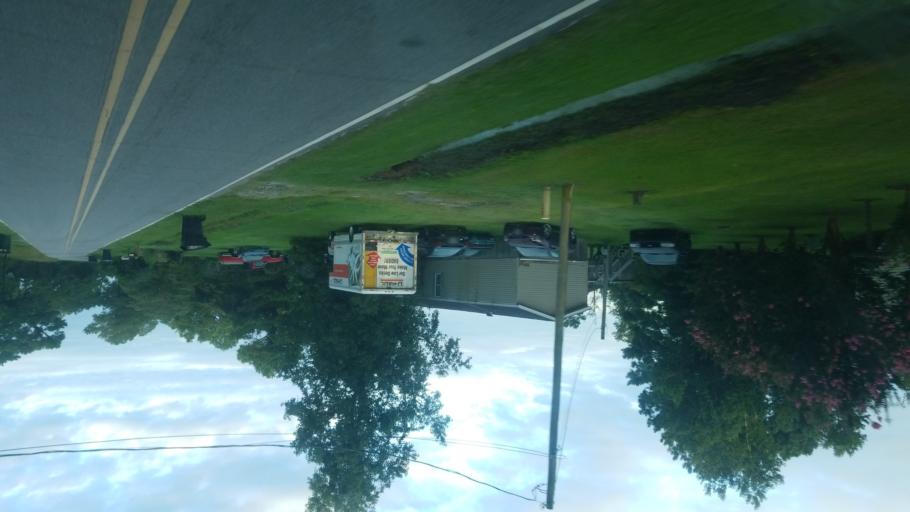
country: US
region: North Carolina
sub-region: Dare County
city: Wanchese
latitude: 35.8417
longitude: -75.6536
